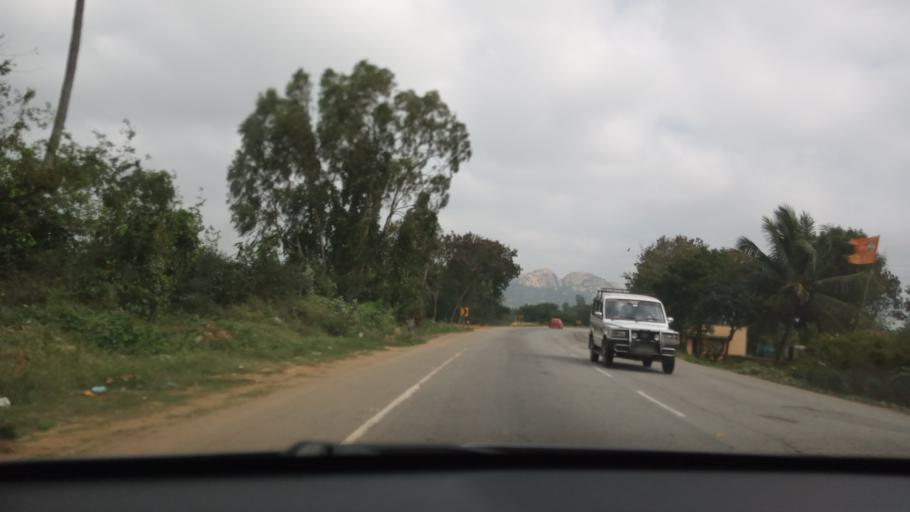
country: IN
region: Karnataka
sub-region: Chikkaballapur
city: Chintamani
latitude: 13.3218
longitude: 77.9828
